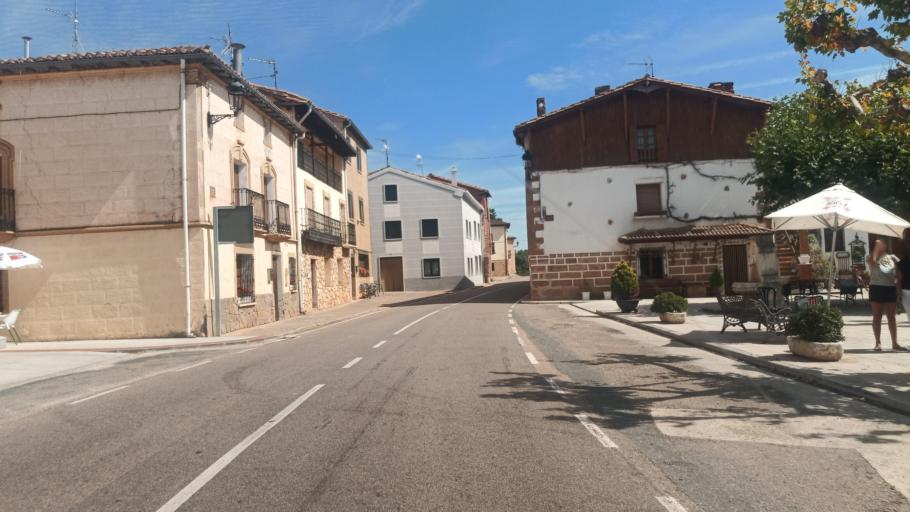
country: ES
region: Castille and Leon
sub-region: Provincia de Burgos
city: Piernigas
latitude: 42.6458
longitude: -3.3914
